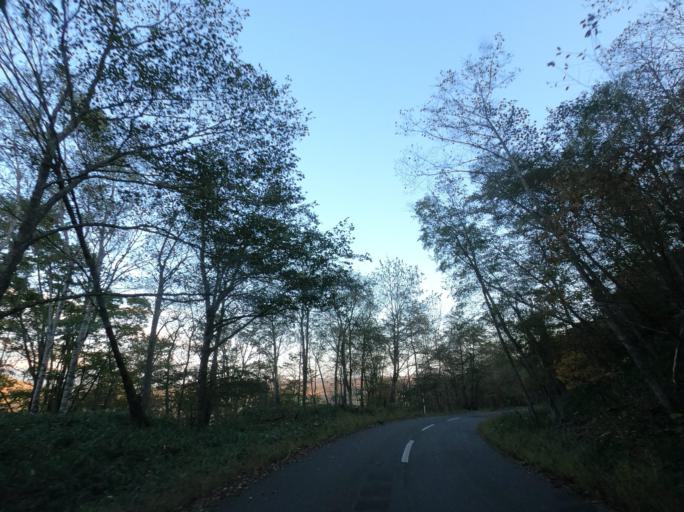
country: JP
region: Hokkaido
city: Kushiro
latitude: 43.1998
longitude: 144.4590
